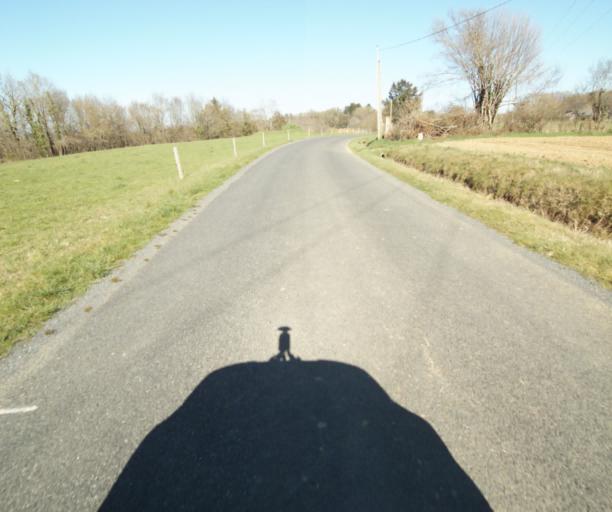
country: FR
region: Limousin
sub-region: Departement de la Correze
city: Chamboulive
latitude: 45.4282
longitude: 1.6481
